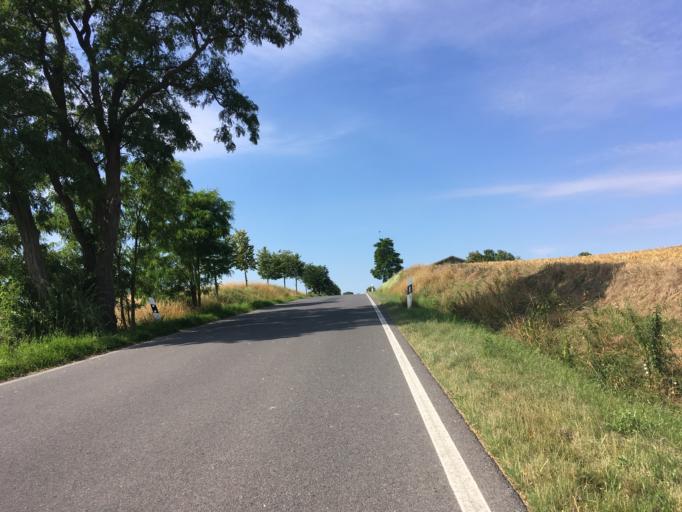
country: DE
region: Brandenburg
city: Gramzow
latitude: 53.2500
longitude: 14.0530
